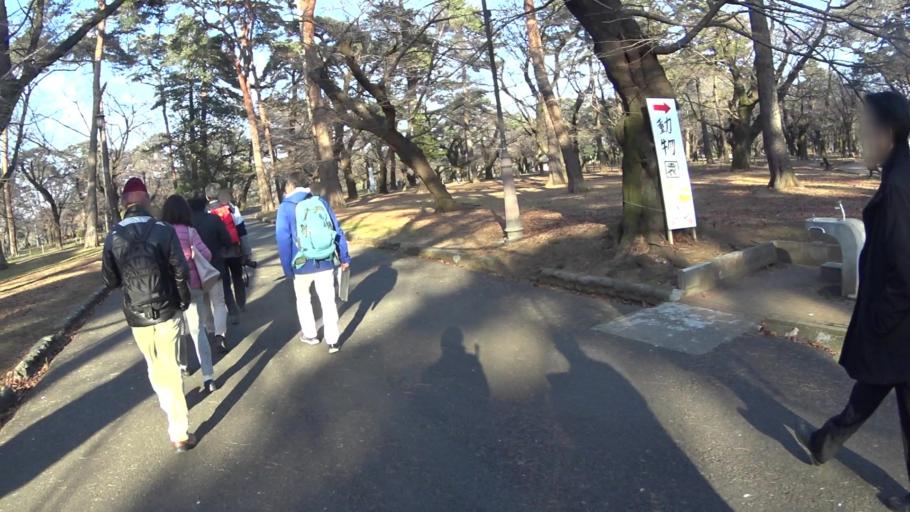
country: JP
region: Saitama
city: Saitama
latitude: 35.9181
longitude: 139.6288
